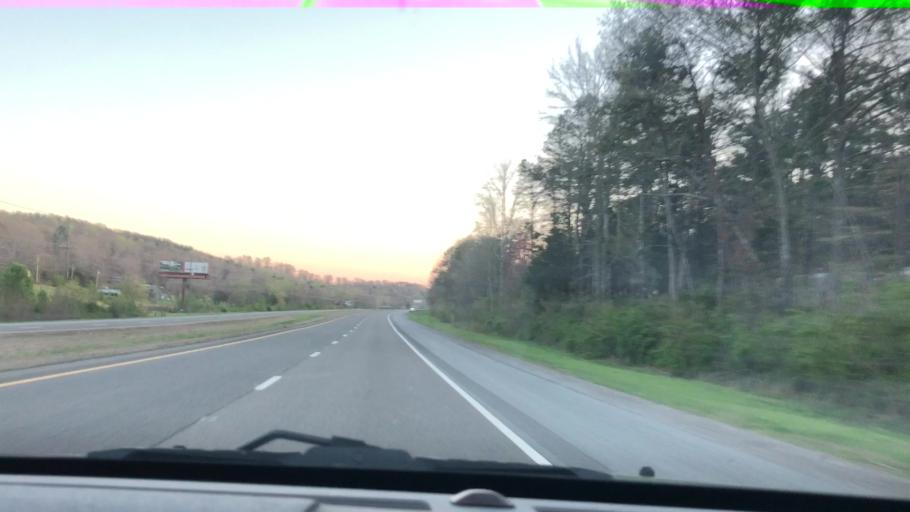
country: US
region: Tennessee
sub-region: Hamilton County
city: Sale Creek
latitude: 35.3609
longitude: -85.1203
